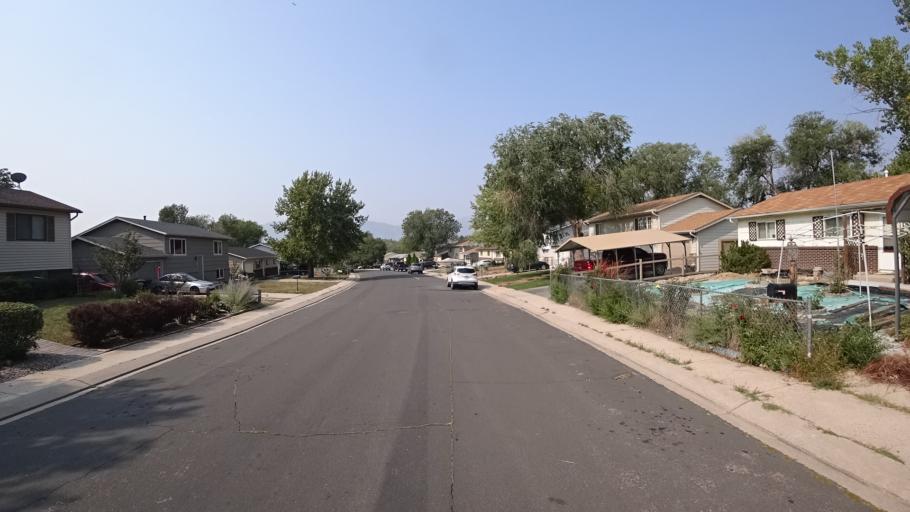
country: US
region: Colorado
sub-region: El Paso County
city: Stratmoor
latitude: 38.8082
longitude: -104.7609
